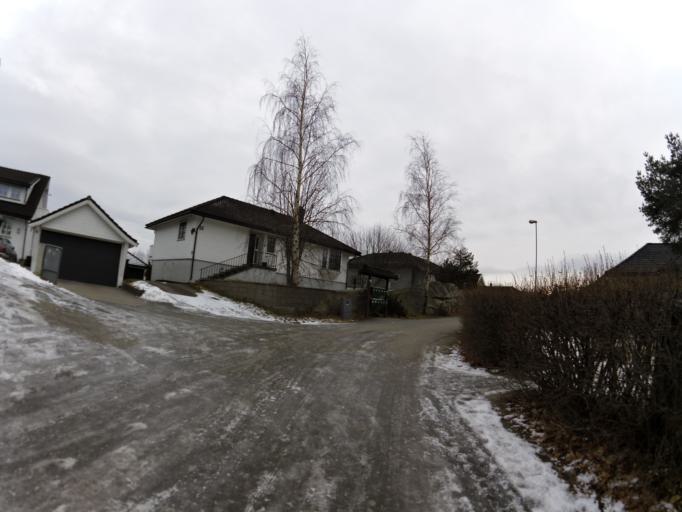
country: NO
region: Ostfold
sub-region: Fredrikstad
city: Fredrikstad
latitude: 59.2013
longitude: 10.8833
